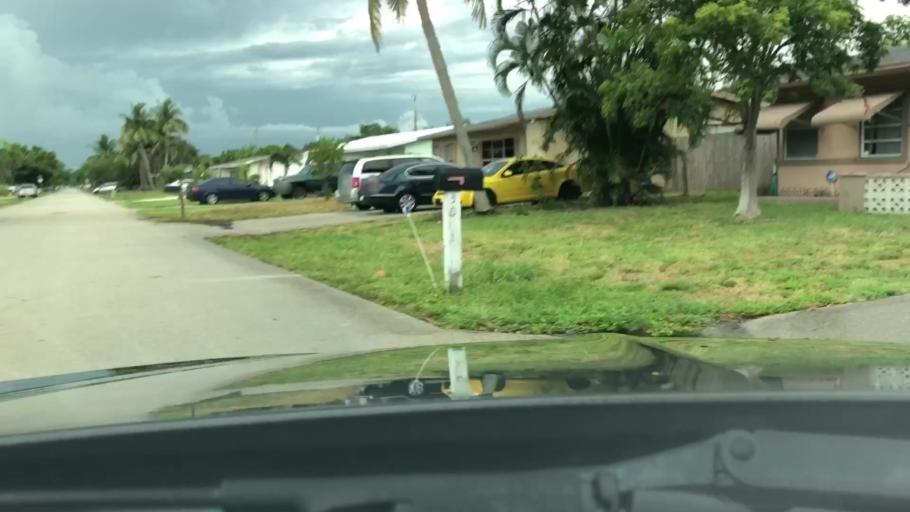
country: US
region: Florida
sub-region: Broward County
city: Pompano Beach Highlands
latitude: 26.2697
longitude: -80.1081
